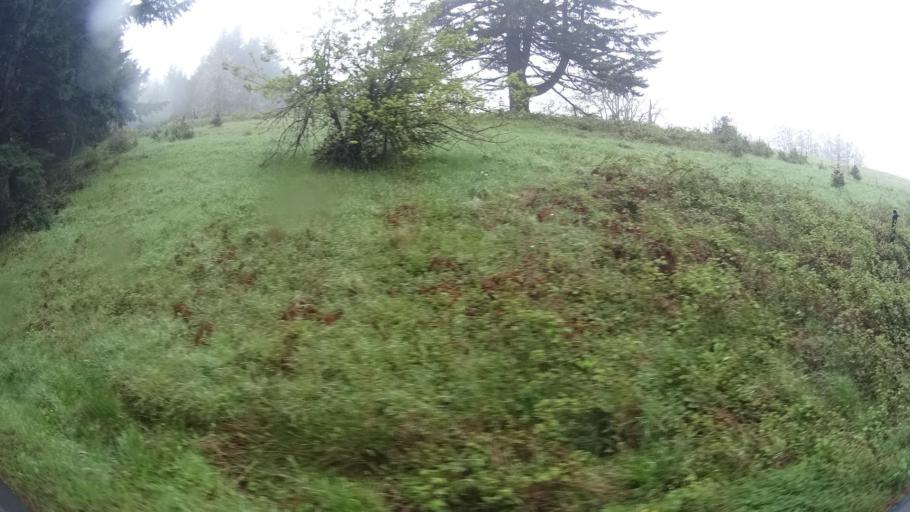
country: US
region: California
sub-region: Humboldt County
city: Westhaven-Moonstone
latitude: 41.1829
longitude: -123.9250
